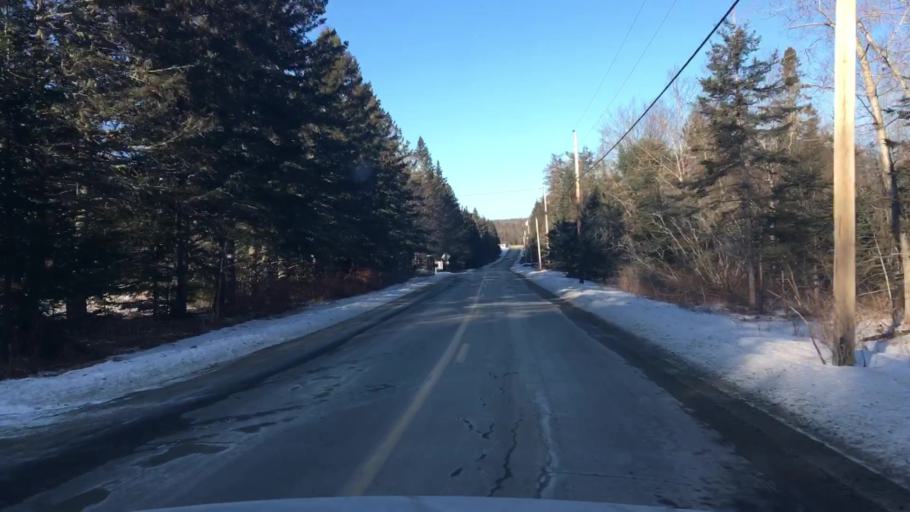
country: US
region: Maine
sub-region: Hancock County
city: Penobscot
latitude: 44.3990
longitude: -68.6975
